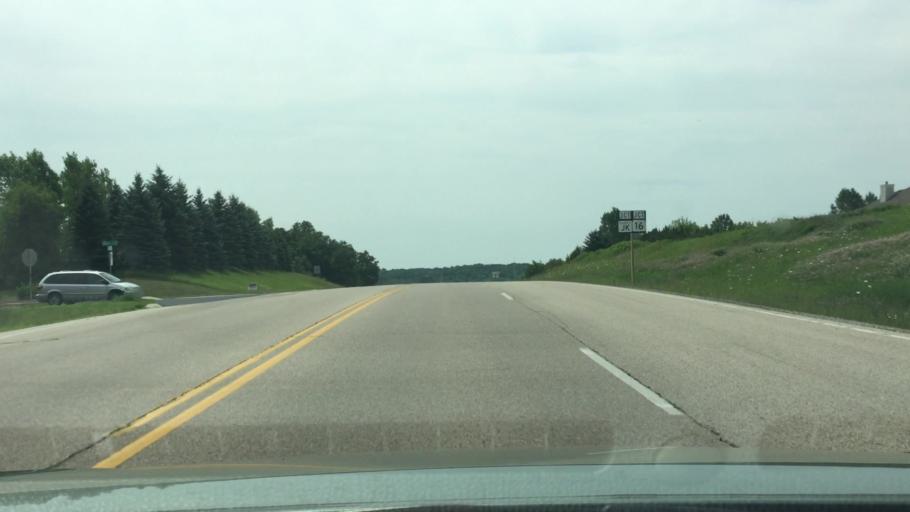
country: US
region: Wisconsin
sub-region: Waukesha County
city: Hartland
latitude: 43.1084
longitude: -88.3135
